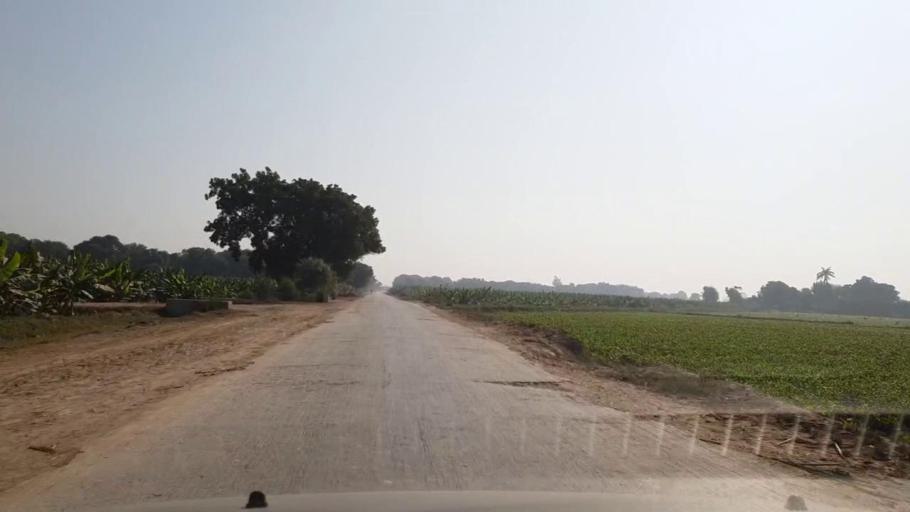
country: PK
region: Sindh
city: Tando Jam
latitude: 25.5263
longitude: 68.5861
